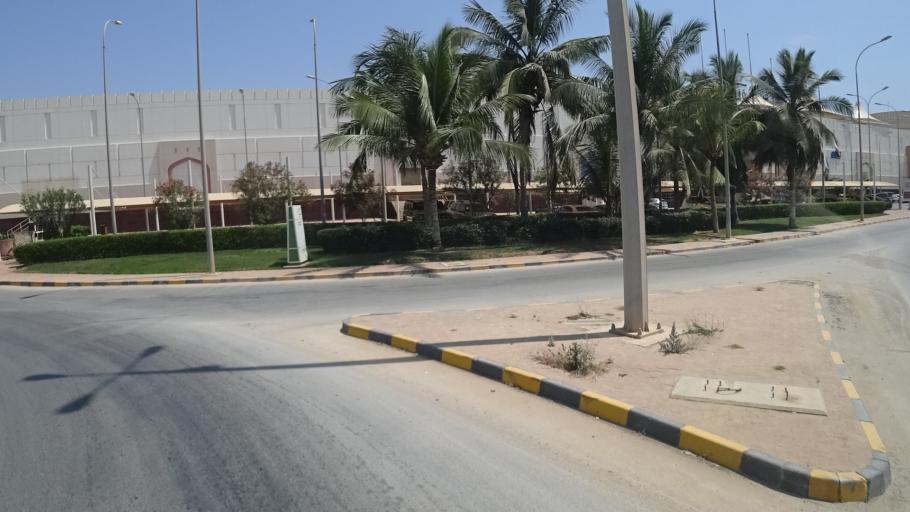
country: OM
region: Zufar
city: Salalah
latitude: 17.0232
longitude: 54.0640
